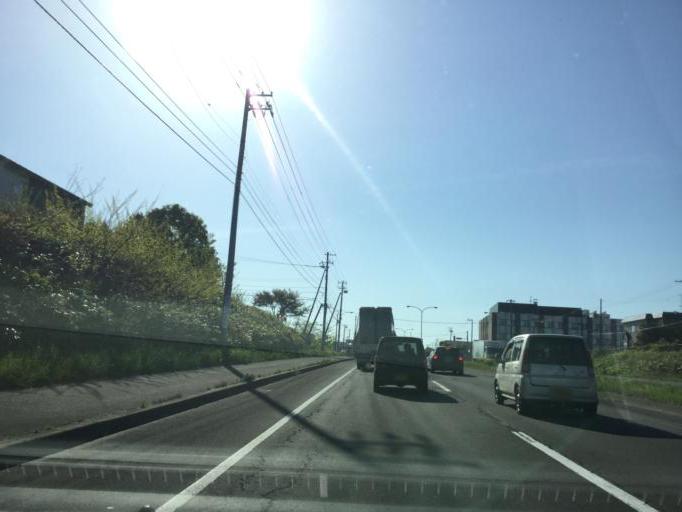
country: JP
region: Hokkaido
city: Kitahiroshima
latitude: 43.0162
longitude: 141.4952
